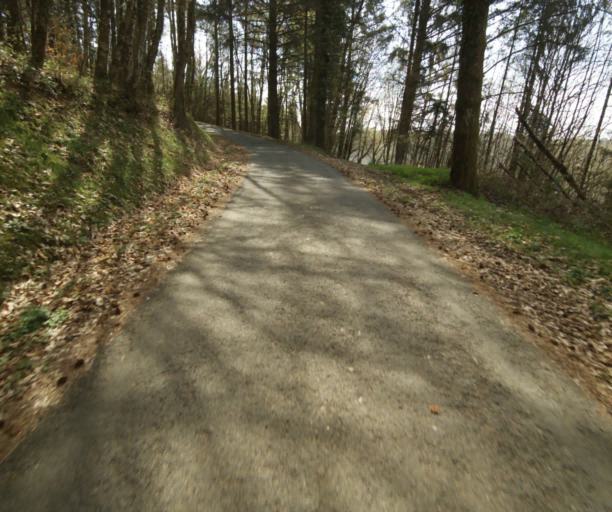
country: FR
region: Limousin
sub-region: Departement de la Correze
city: Naves
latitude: 45.3653
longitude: 1.7922
